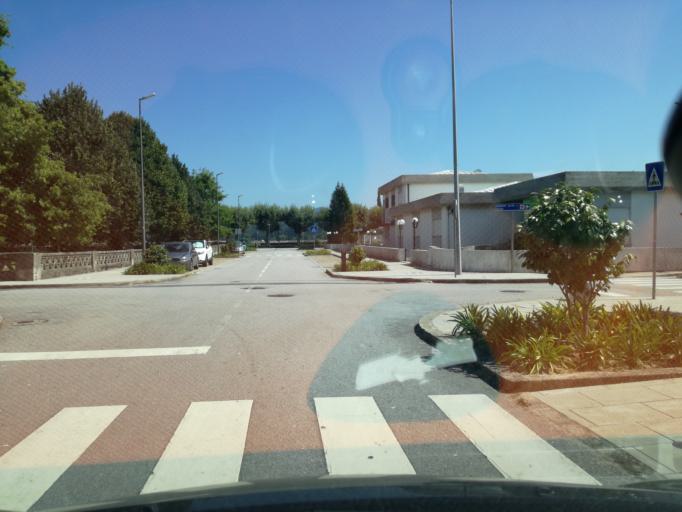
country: ES
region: Galicia
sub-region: Provincia de Pontevedra
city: A Guarda
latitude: 41.8761
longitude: -8.8352
